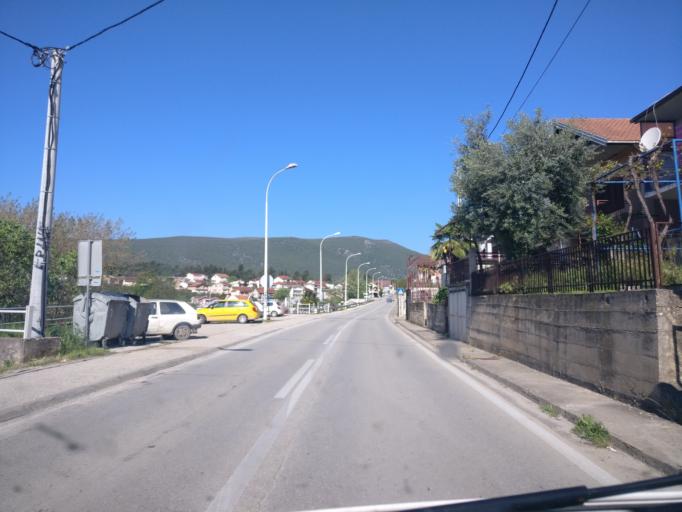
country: BA
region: Federation of Bosnia and Herzegovina
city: Capljina
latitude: 43.1184
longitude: 17.6924
